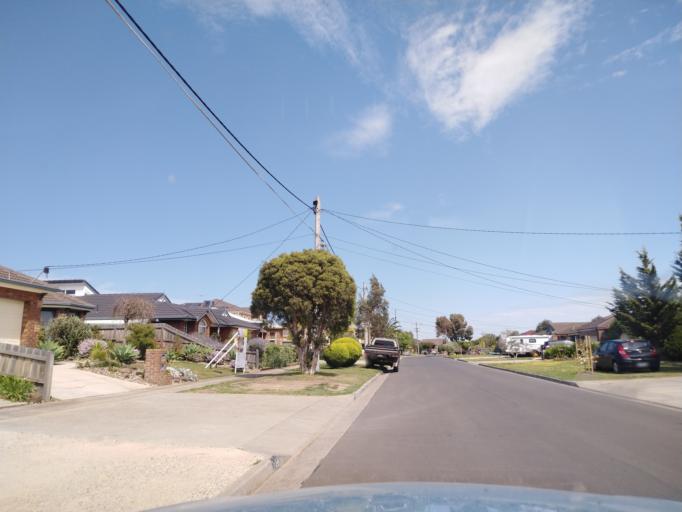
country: AU
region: Victoria
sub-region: Wyndham
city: Hoppers Crossing
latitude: -37.8609
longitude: 144.7128
